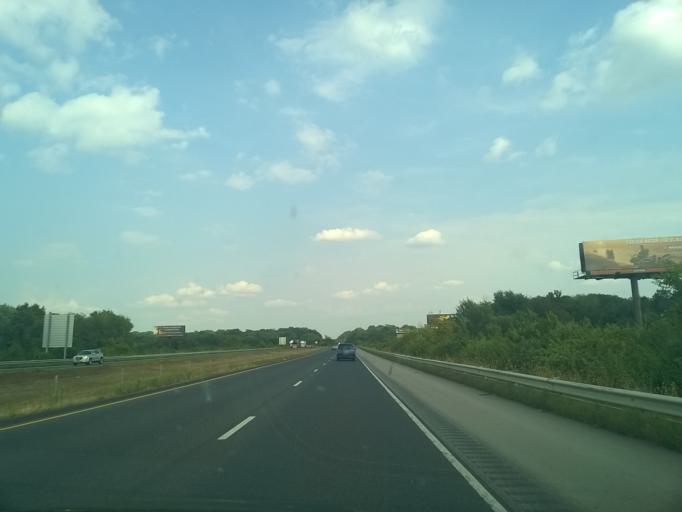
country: US
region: Indiana
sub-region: Vigo County
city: Terre Haute
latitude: 39.4309
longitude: -87.3821
